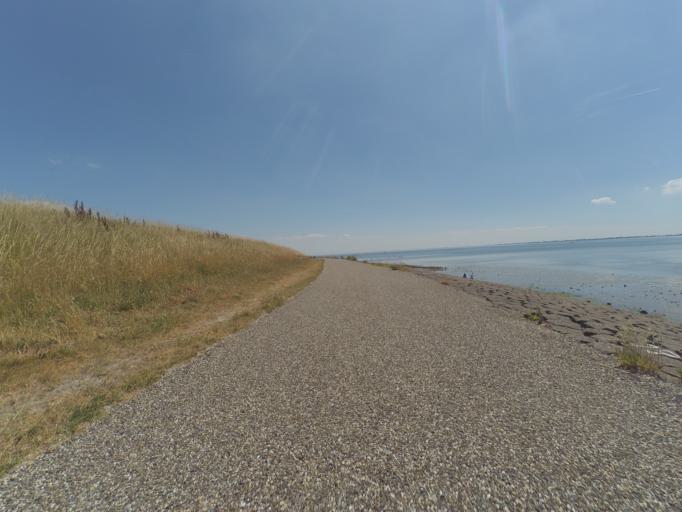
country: NL
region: Zeeland
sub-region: Gemeente Reimerswaal
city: Yerseke
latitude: 51.5348
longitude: 4.0643
